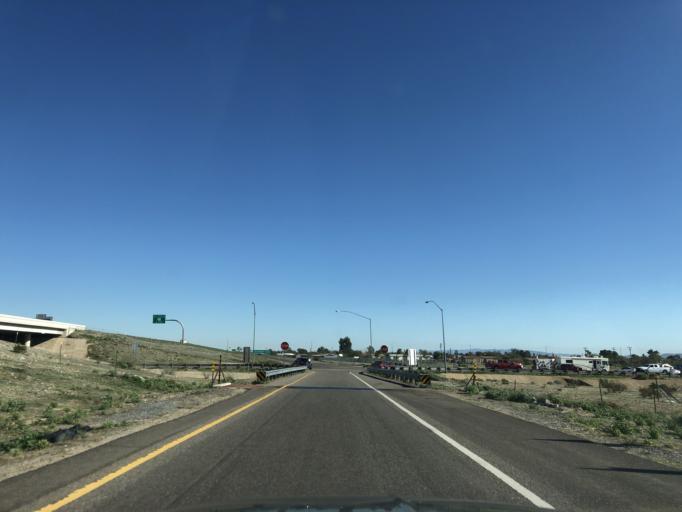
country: US
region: Arizona
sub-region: Maricopa County
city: Citrus Park
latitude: 33.4619
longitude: -112.4799
